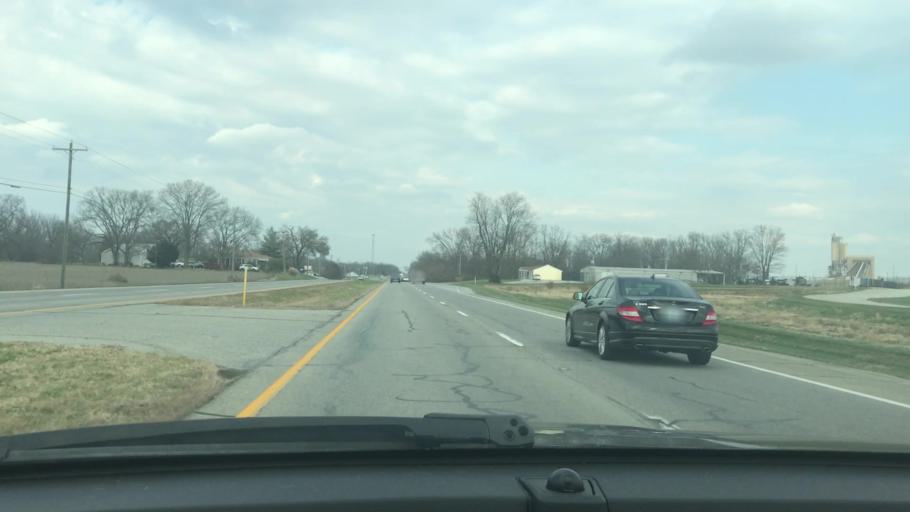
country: US
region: Indiana
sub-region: Clark County
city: Charlestown
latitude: 38.4058
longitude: -85.6754
